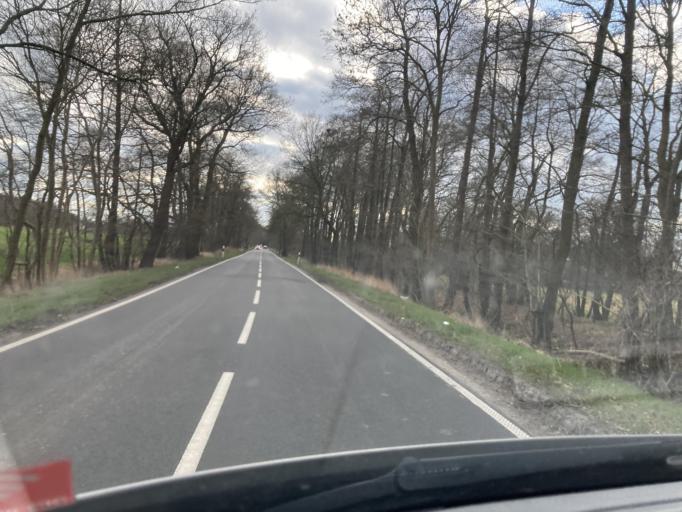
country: DE
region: Lower Saxony
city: Nortmoor
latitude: 53.1869
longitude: 7.5981
